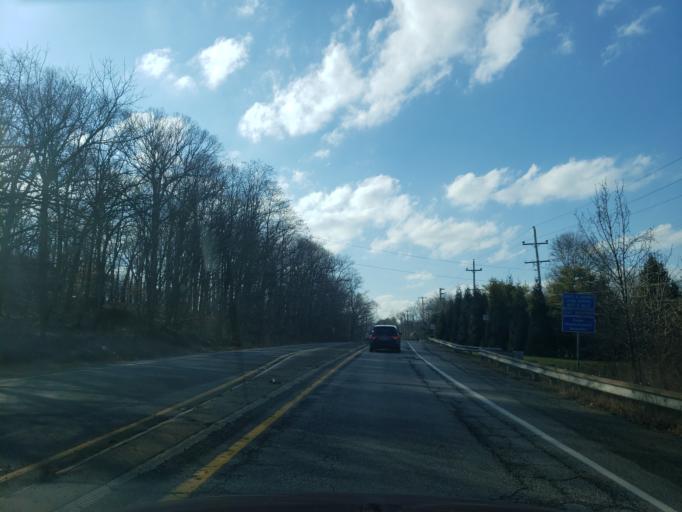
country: US
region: Pennsylvania
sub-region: Bucks County
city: Doylestown
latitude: 40.3253
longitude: -75.0628
